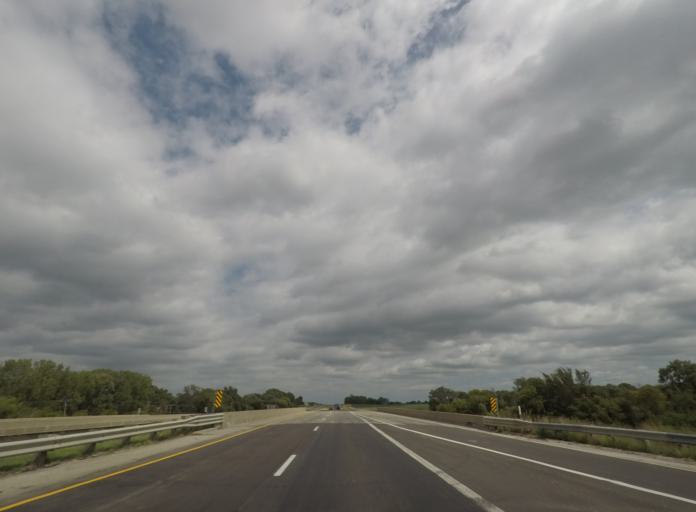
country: US
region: Iowa
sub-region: Linn County
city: Ely
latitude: 41.9265
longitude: -91.6331
